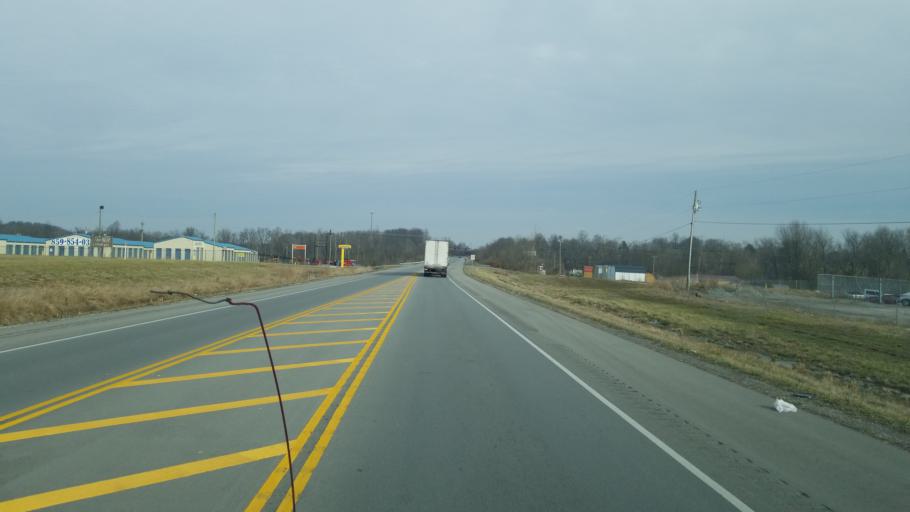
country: US
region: Kentucky
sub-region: Boyle County
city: Junction City
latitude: 37.5639
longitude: -84.7977
